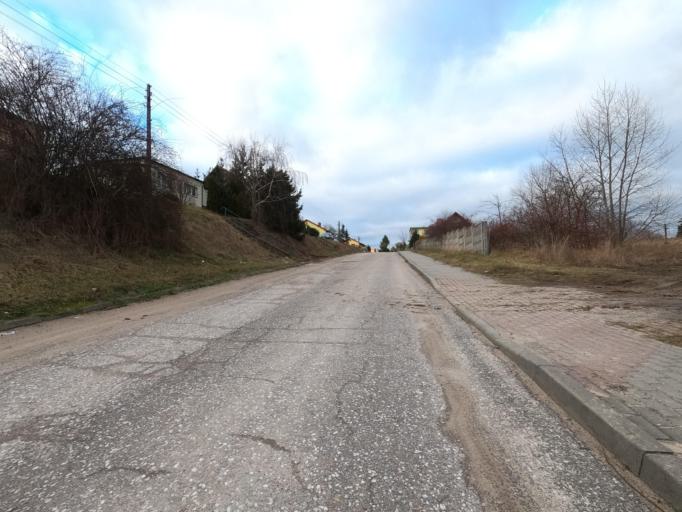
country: PL
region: Greater Poland Voivodeship
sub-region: Powiat pilski
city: Bialosliwie
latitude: 53.1007
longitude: 17.1220
